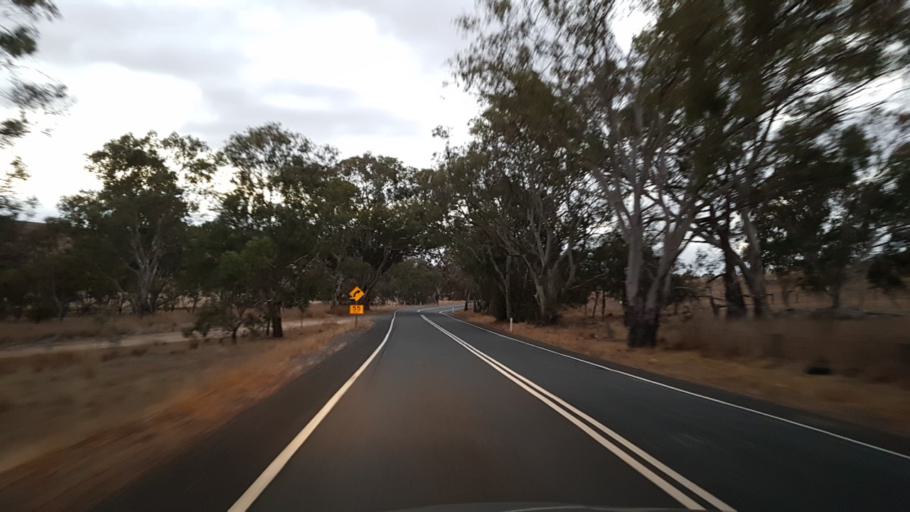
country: AU
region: South Australia
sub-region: Mount Barker
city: Nairne
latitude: -35.0329
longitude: 138.9709
